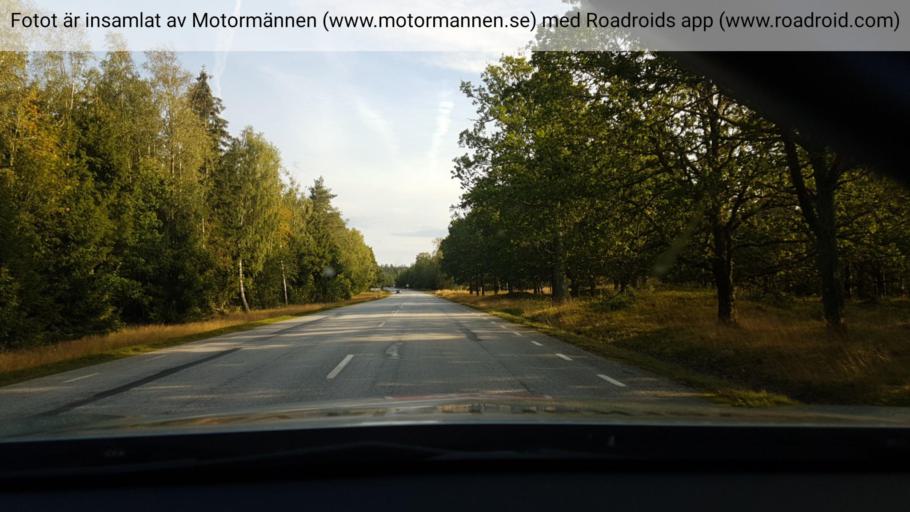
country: SE
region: Vaestra Goetaland
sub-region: Uddevalla Kommun
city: Ljungskile
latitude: 58.1296
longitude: 11.9815
